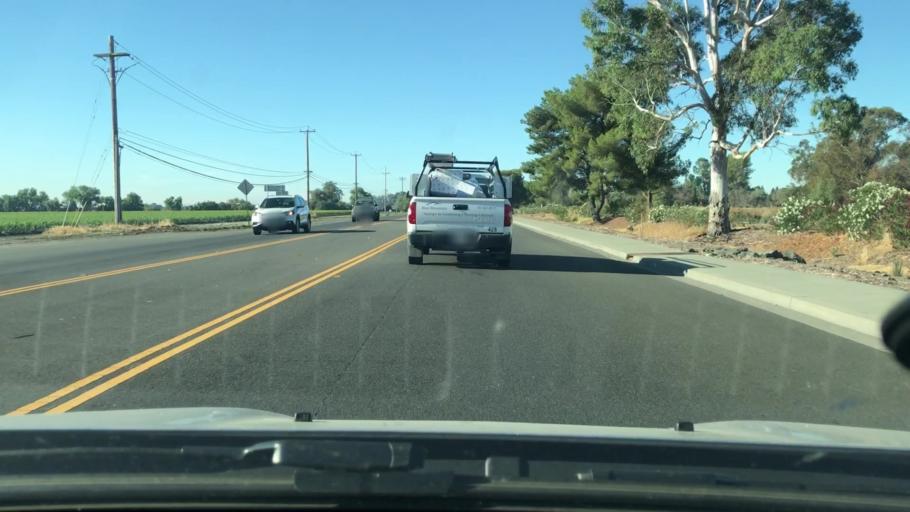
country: US
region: California
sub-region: Solano County
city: Hartley
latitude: 38.3733
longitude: -121.9339
